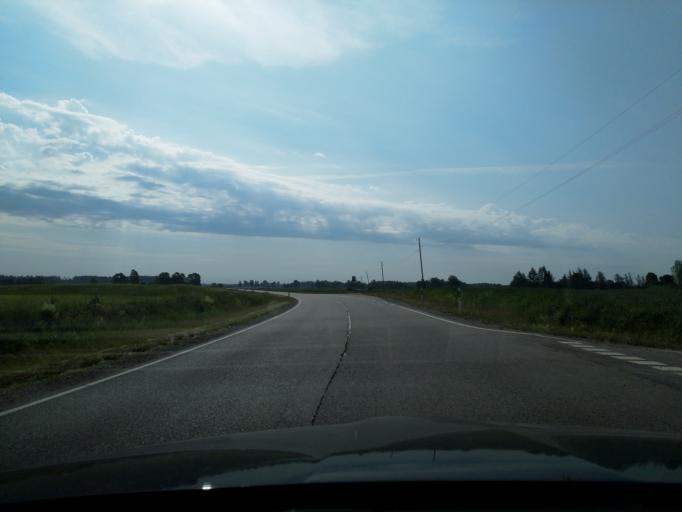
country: LV
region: Talsu Rajons
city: Sabile
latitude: 56.9376
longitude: 22.4969
